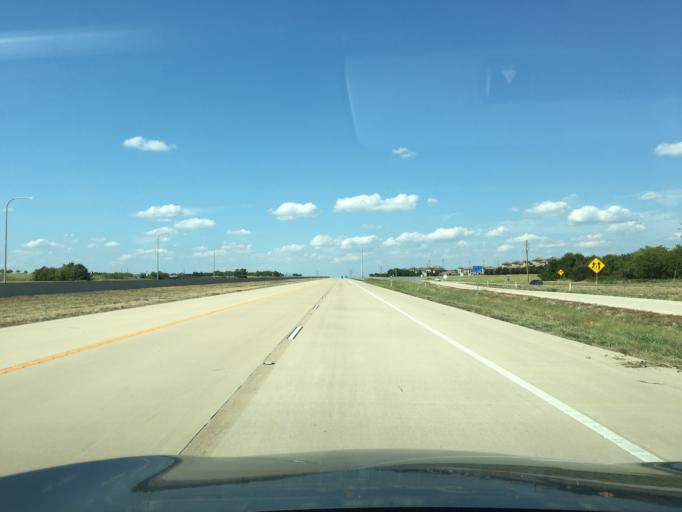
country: US
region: Texas
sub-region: Tarrant County
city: Mansfield
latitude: 32.5627
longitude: -97.0845
